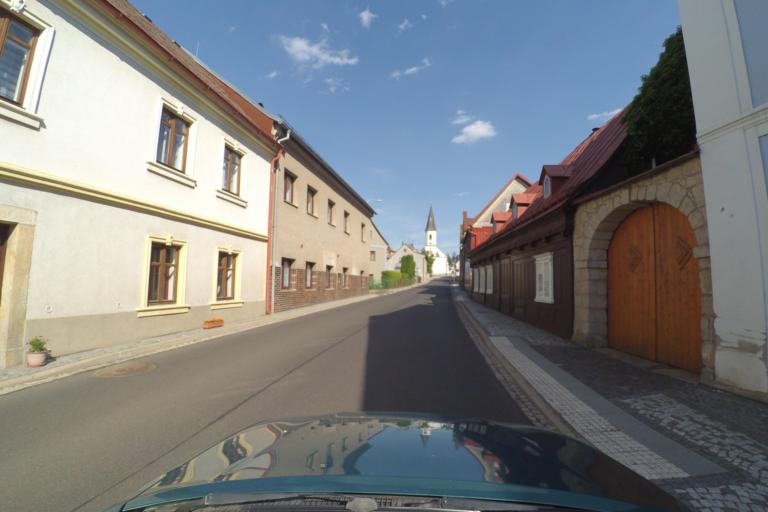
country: CZ
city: Osecna
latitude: 50.6954
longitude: 14.9190
